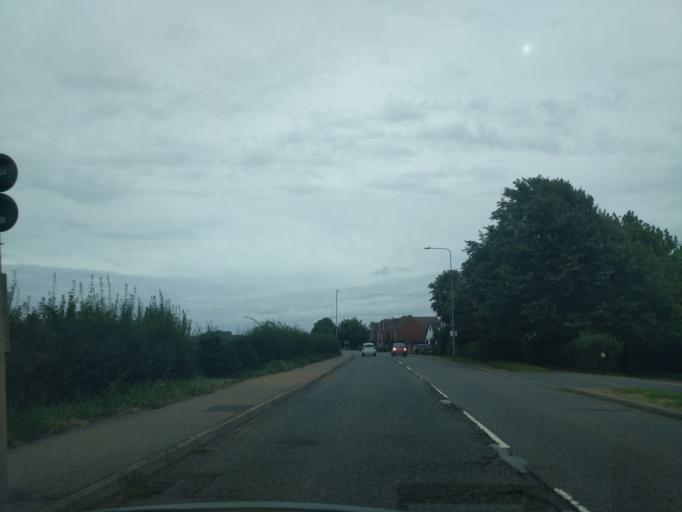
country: GB
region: England
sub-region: Lincolnshire
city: Great Gonerby
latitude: 52.9178
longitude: -0.6707
